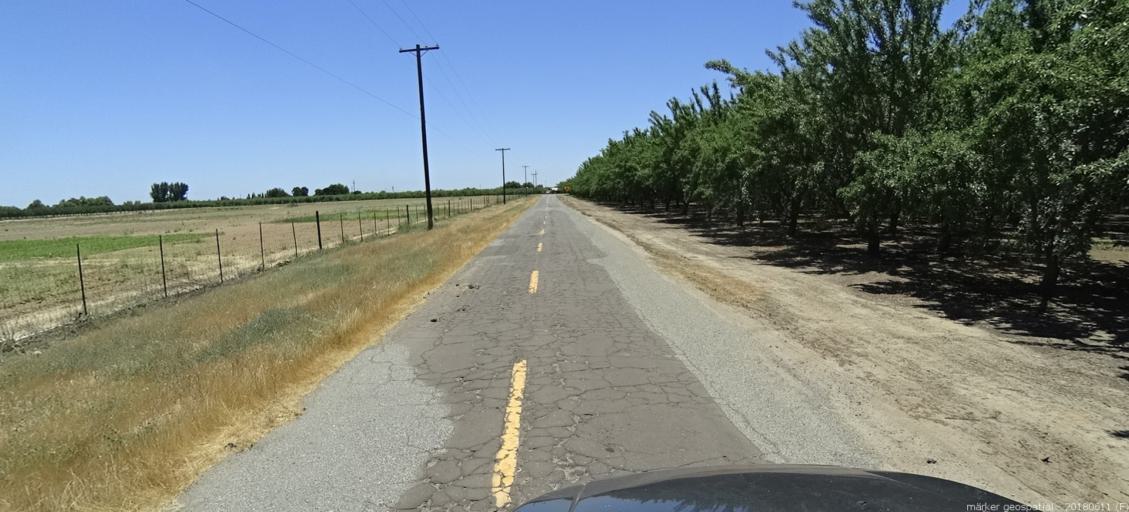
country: US
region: California
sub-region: Madera County
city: Fairmead
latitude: 36.9991
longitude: -120.1933
